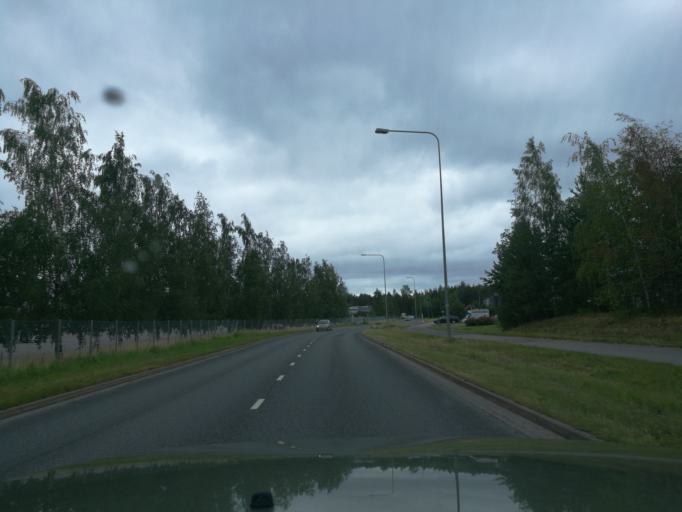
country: FI
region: Uusimaa
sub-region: Helsinki
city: Vantaa
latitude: 60.3416
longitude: 25.0107
